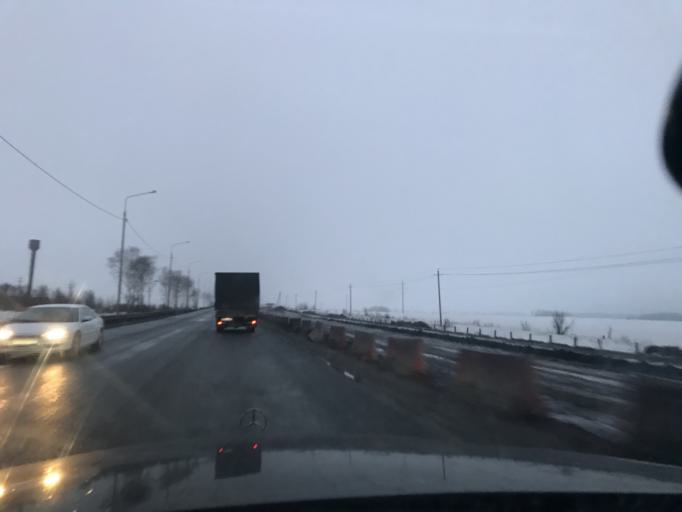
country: RU
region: Vladimir
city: Novovyazniki
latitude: 56.2187
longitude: 42.1993
